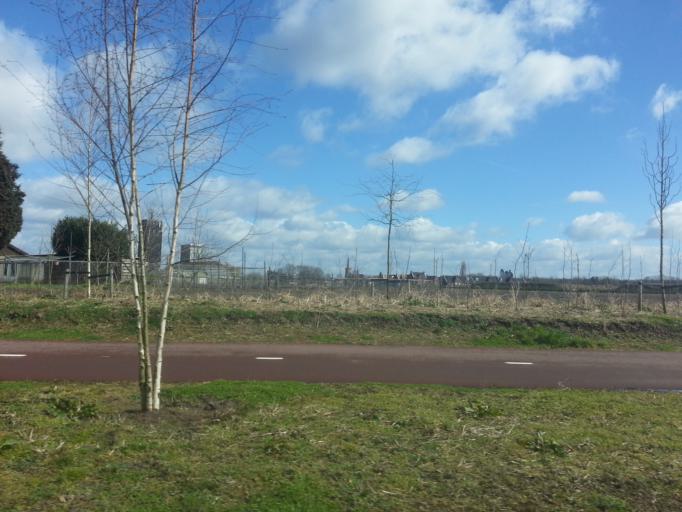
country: NL
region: North Brabant
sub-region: Gemeente Veldhoven
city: Oerle
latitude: 51.4173
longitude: 5.3623
